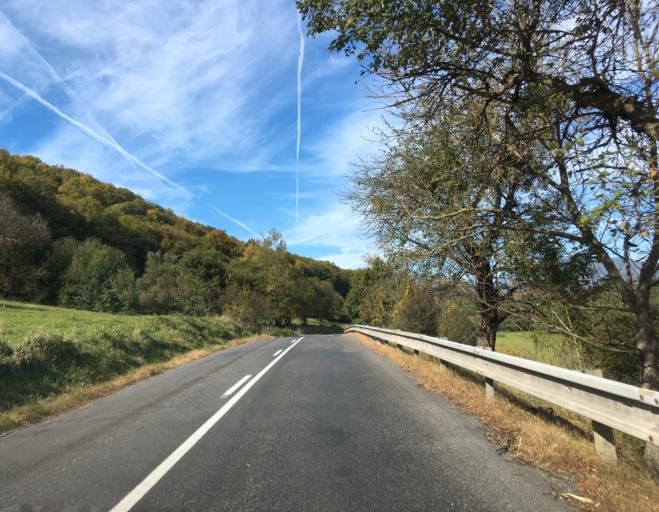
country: SK
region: Banskobystricky
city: Svaety Anton
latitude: 48.3438
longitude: 18.9357
